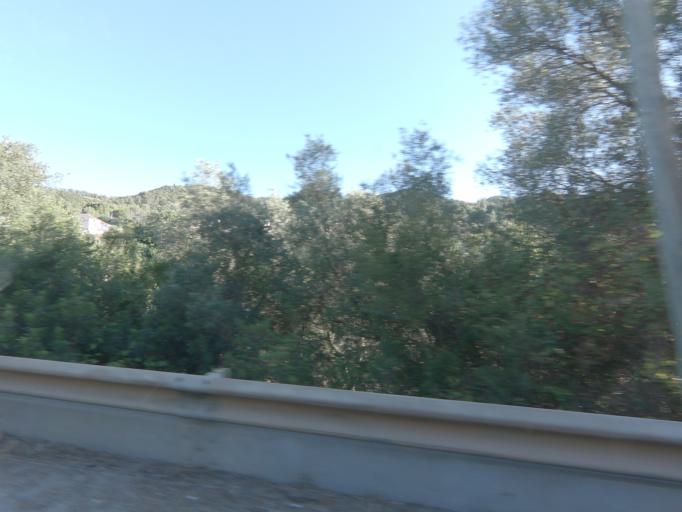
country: PT
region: Setubal
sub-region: Palmela
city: Quinta do Anjo
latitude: 38.5047
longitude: -8.9536
